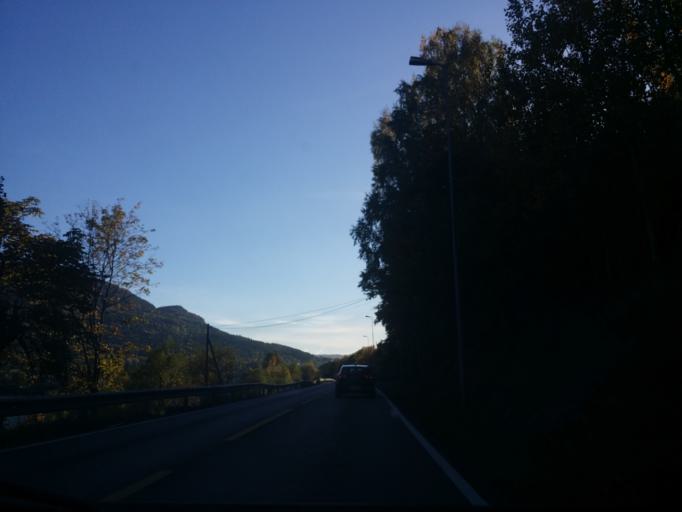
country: NO
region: Buskerud
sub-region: Hole
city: Vik
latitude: 60.0692
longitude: 10.3008
